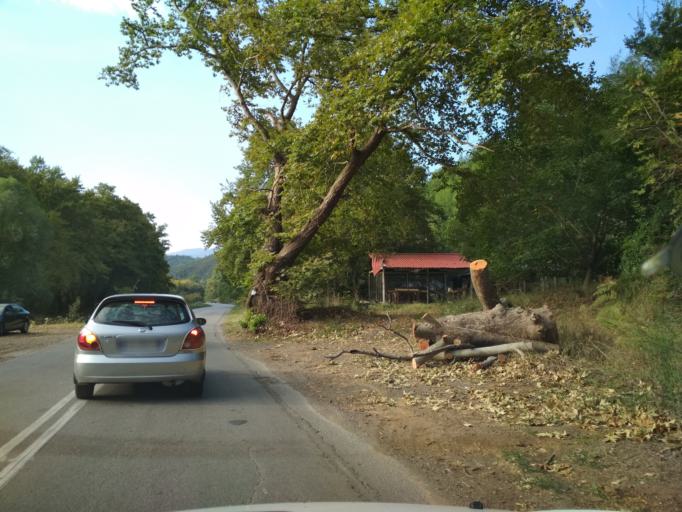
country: GR
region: Central Greece
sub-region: Nomos Evvoias
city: Mantoudi
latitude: 38.7830
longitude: 23.4703
